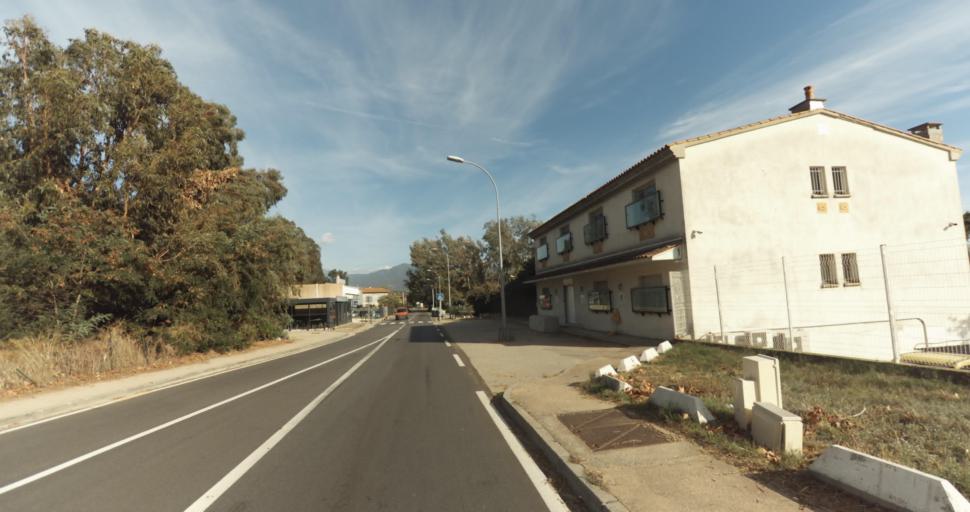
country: FR
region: Corsica
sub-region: Departement de la Corse-du-Sud
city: Afa
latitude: 41.9283
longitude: 8.7942
